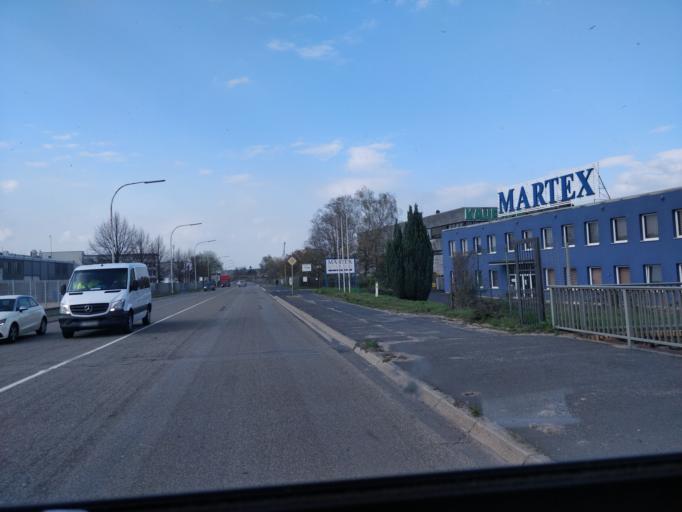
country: DE
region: North Rhine-Westphalia
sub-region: Regierungsbezirk Koln
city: Frechen
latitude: 50.9165
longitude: 6.8268
